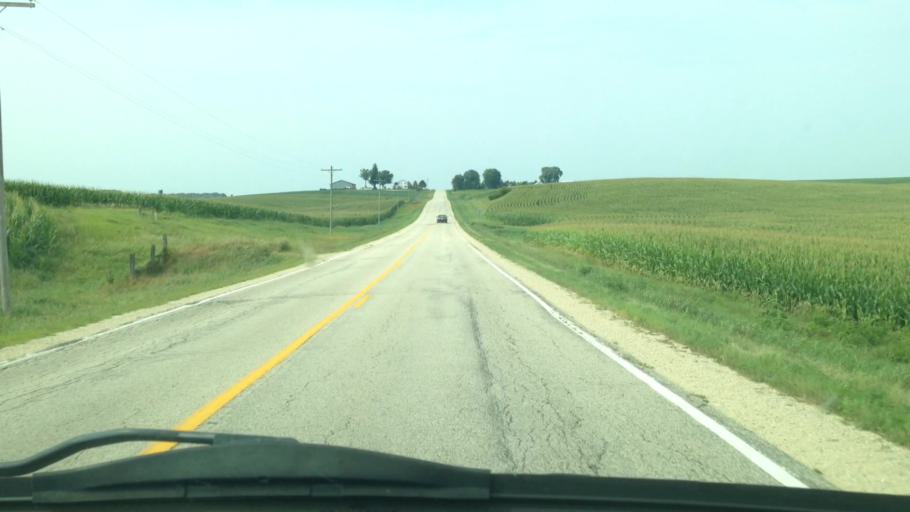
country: US
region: Minnesota
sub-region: Winona County
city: Lewiston
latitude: 43.8859
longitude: -91.9594
